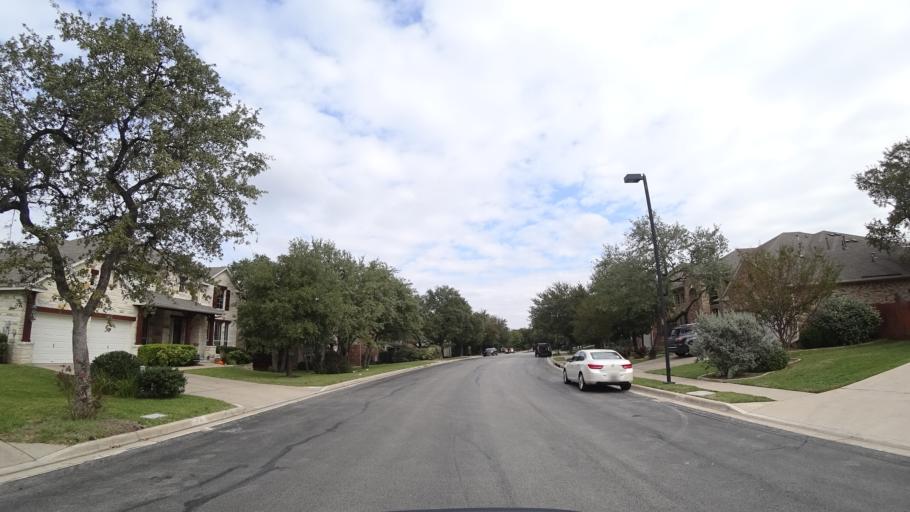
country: US
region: Texas
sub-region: Travis County
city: Shady Hollow
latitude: 30.1882
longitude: -97.9051
